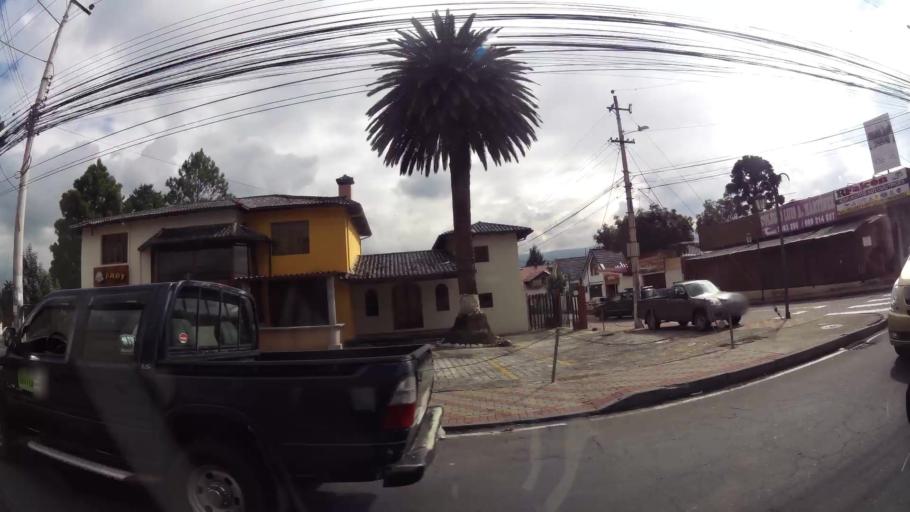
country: EC
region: Pichincha
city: Sangolqui
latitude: -0.3109
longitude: -78.4517
